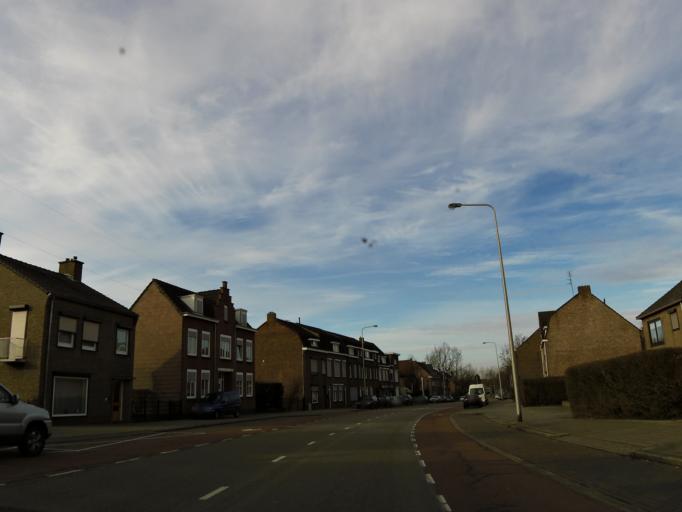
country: NL
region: Limburg
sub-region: Gemeente Heerlen
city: Nieuw-Lotbroek
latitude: 50.9162
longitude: 5.9522
